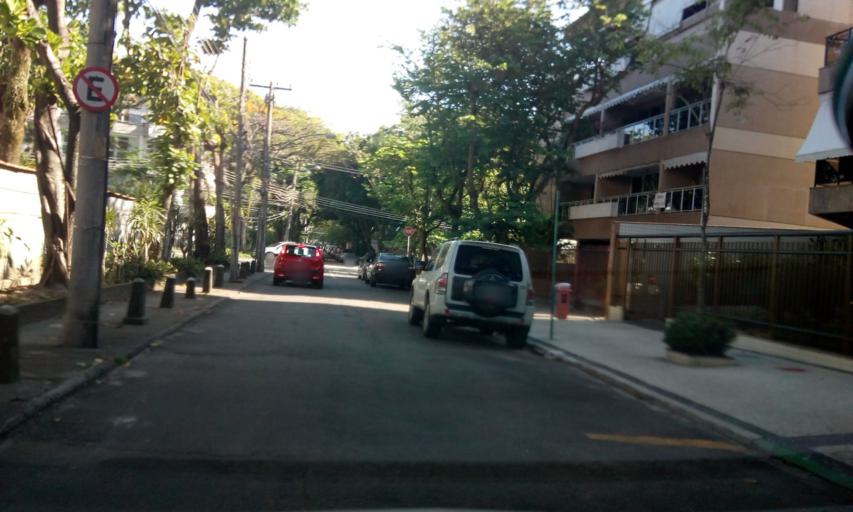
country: BR
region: Rio de Janeiro
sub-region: Rio De Janeiro
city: Rio de Janeiro
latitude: -23.0123
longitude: -43.3142
